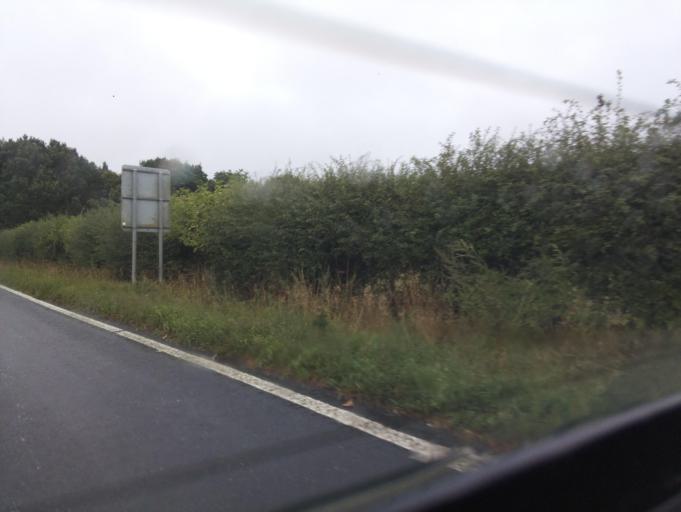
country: GB
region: England
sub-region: North Yorkshire
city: Pannal
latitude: 53.9291
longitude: -1.5363
